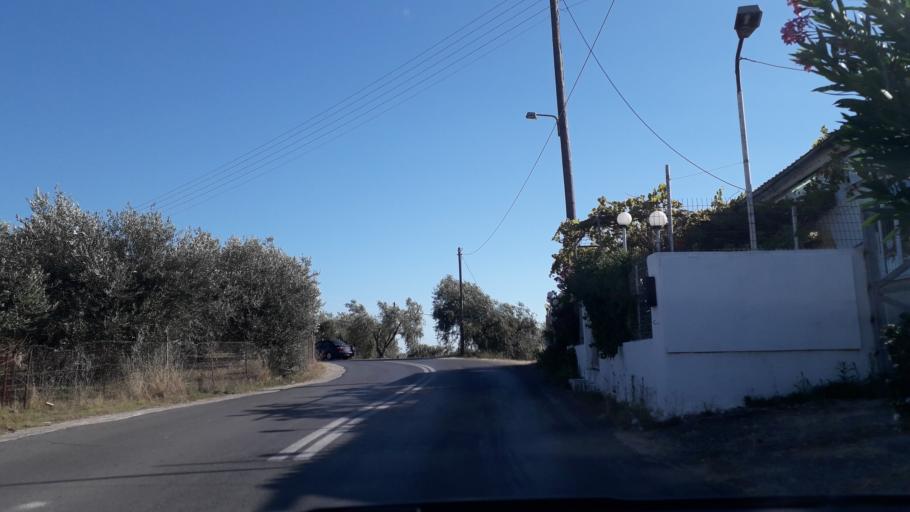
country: GR
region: Ionian Islands
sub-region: Nomos Kerkyras
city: Perivoli
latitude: 39.4362
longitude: 19.9514
